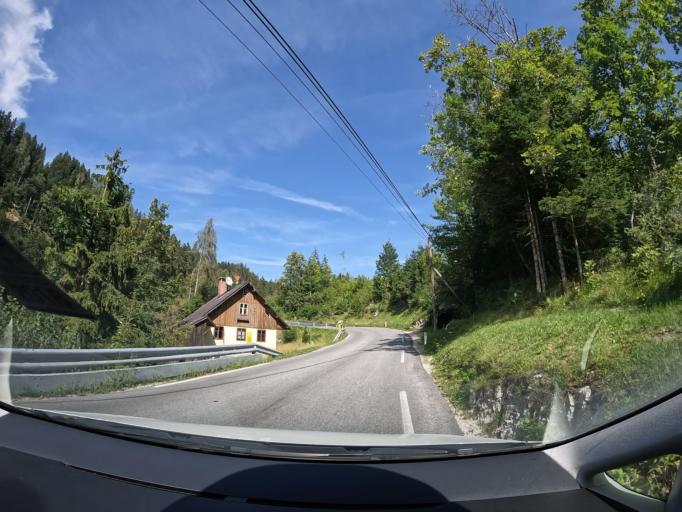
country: AT
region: Carinthia
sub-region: Politischer Bezirk Klagenfurt Land
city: Schiefling am See
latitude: 46.5899
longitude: 14.0684
